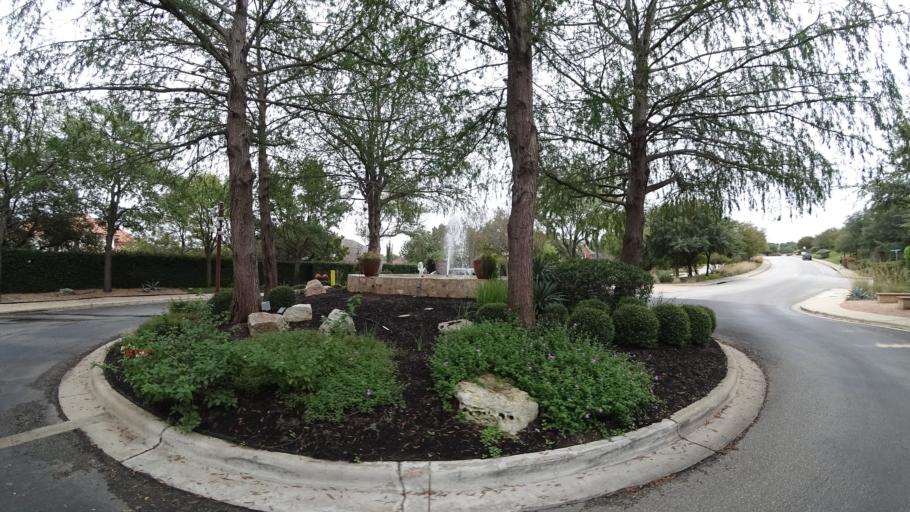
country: US
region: Texas
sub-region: Travis County
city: Bee Cave
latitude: 30.3210
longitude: -97.9153
